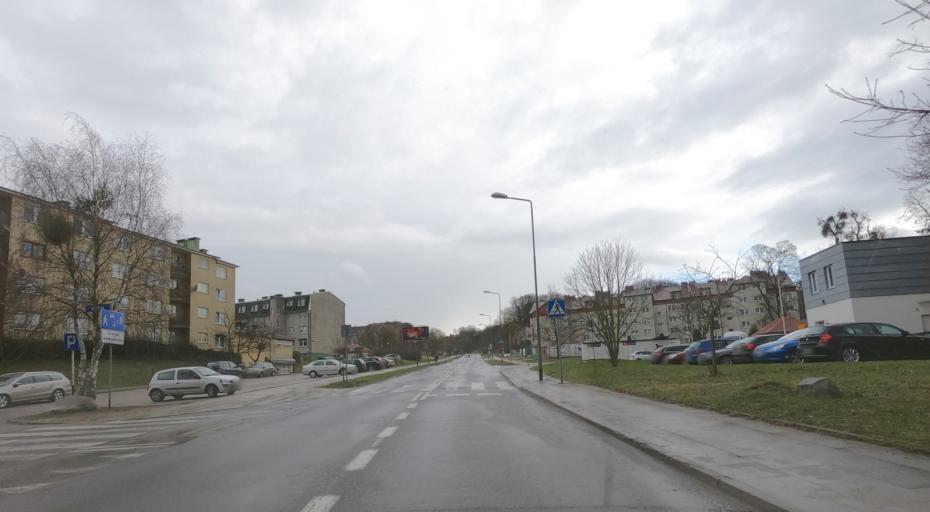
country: PL
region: West Pomeranian Voivodeship
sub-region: Szczecin
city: Szczecin
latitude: 53.3675
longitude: 14.6467
